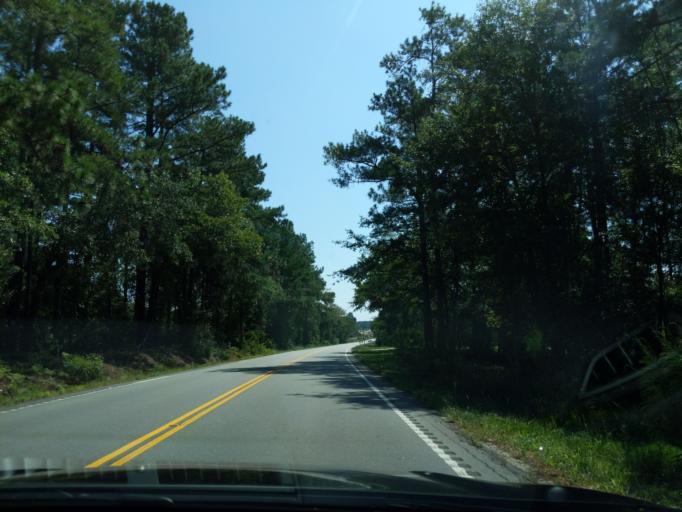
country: US
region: South Carolina
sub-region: Lexington County
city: Red Bank
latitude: 33.9300
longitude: -81.3187
